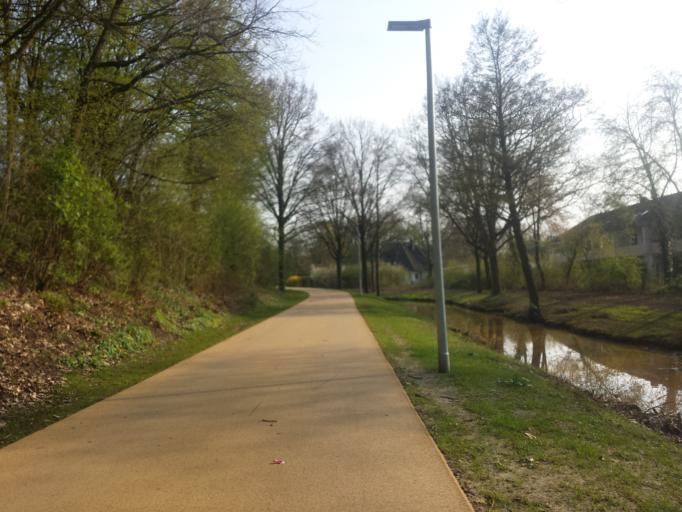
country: DE
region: Lower Saxony
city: Lilienthal
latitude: 53.0677
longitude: 8.9022
